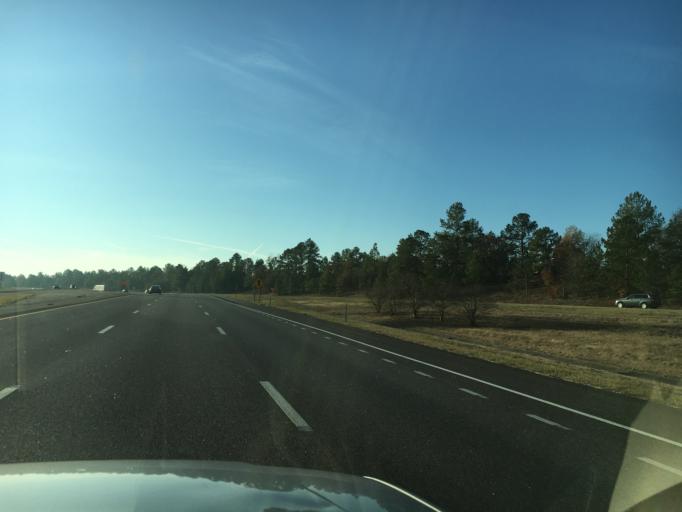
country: US
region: South Carolina
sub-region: Lexington County
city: Pineridge
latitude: 33.9243
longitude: -81.0689
